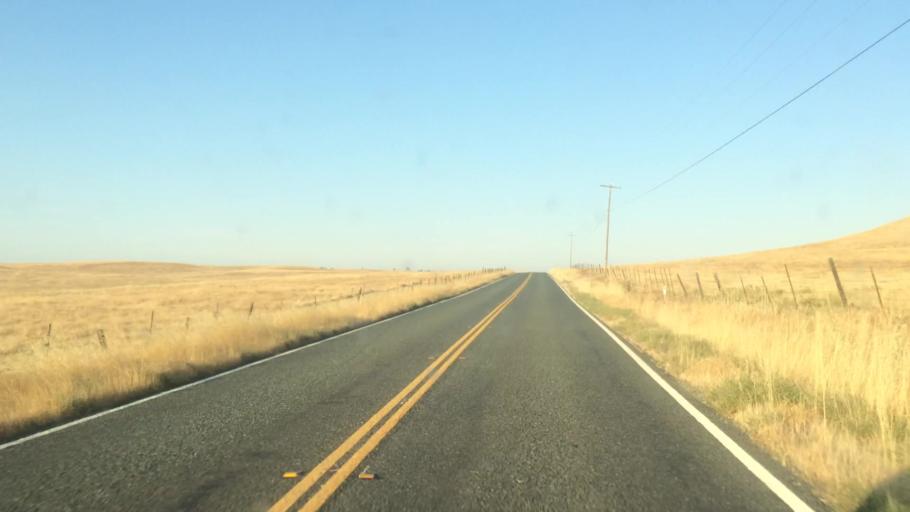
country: US
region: California
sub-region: Sacramento County
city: Clay
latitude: 38.3536
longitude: -121.0786
